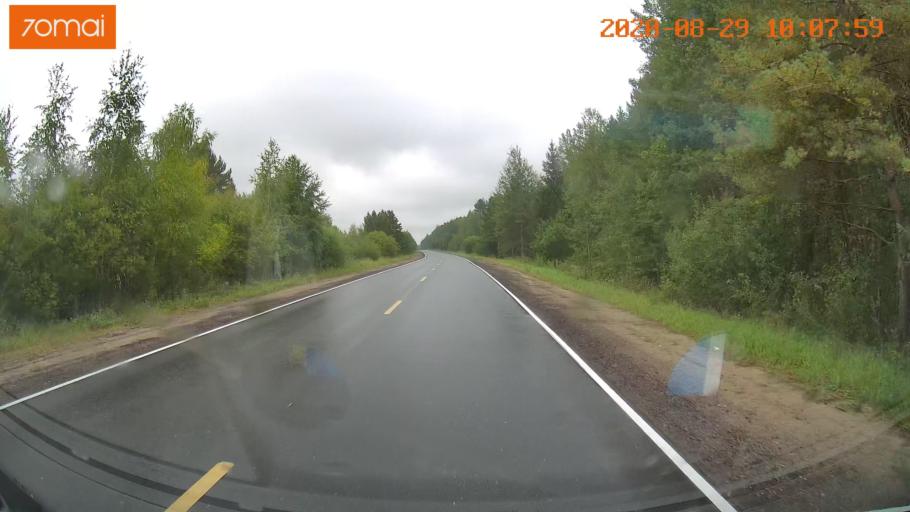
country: RU
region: Ivanovo
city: Kuznechikha
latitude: 57.3775
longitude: 42.5789
